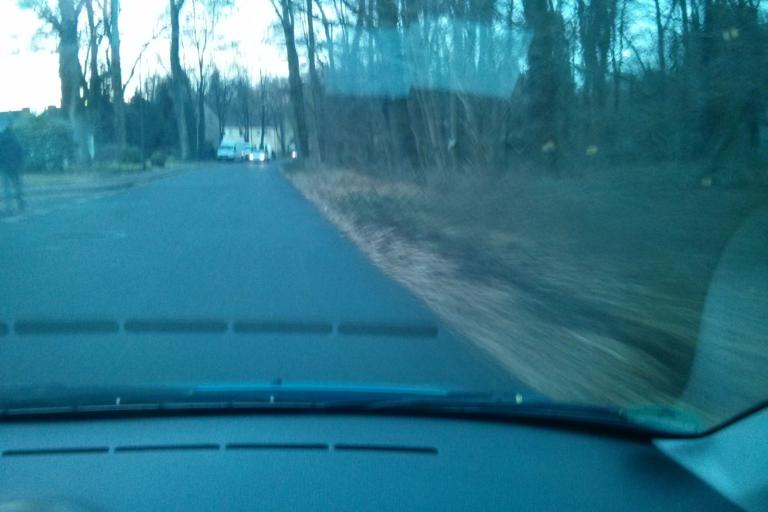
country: DE
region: North Rhine-Westphalia
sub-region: Regierungsbezirk Koln
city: Troisdorf
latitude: 50.8198
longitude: 7.1763
